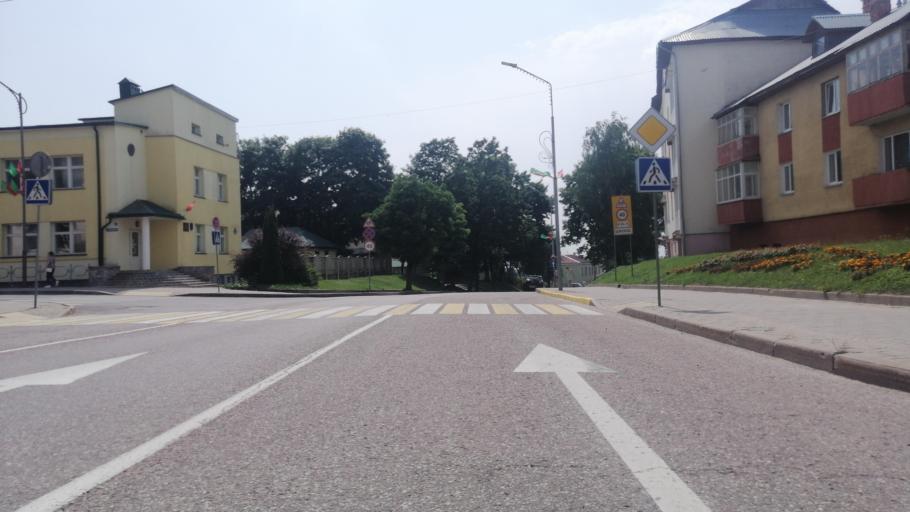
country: BY
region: Grodnenskaya
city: Navahrudak
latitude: 53.5939
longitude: 25.8217
